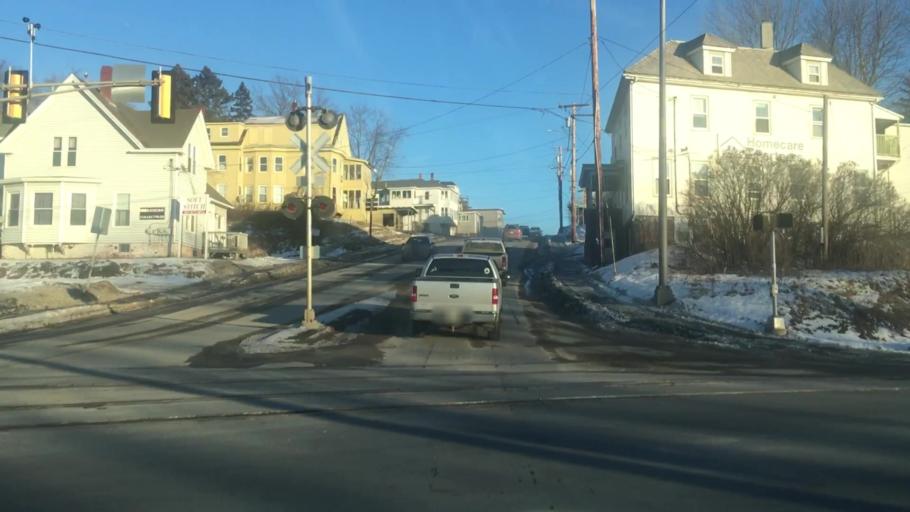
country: US
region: Maine
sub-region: Kennebec County
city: Winslow
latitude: 44.5473
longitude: -69.6254
